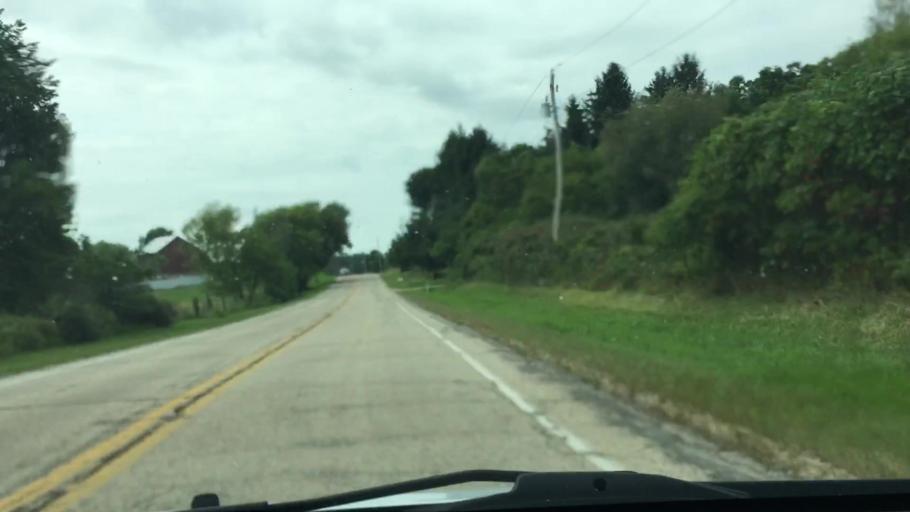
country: US
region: Wisconsin
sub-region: Dane County
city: Belleville
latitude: 42.8824
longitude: -89.4815
